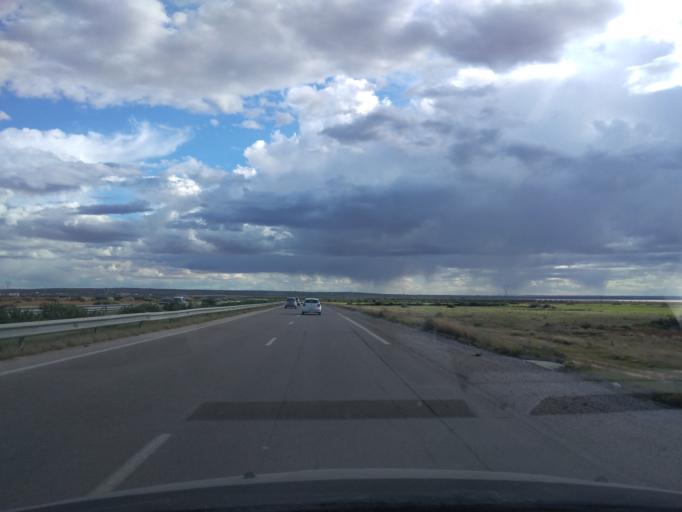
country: TN
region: Al Munastir
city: Manzil Kamil
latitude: 35.5043
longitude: 10.6252
